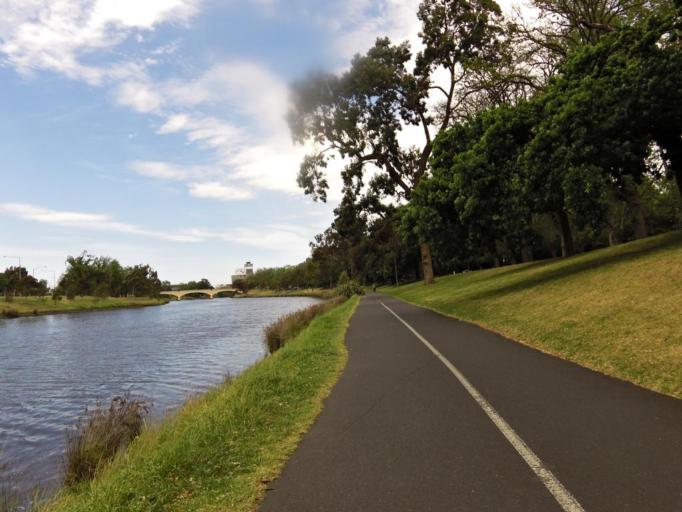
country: AU
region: Victoria
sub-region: Melbourne
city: East Melbourne
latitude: -37.8263
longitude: 144.9797
